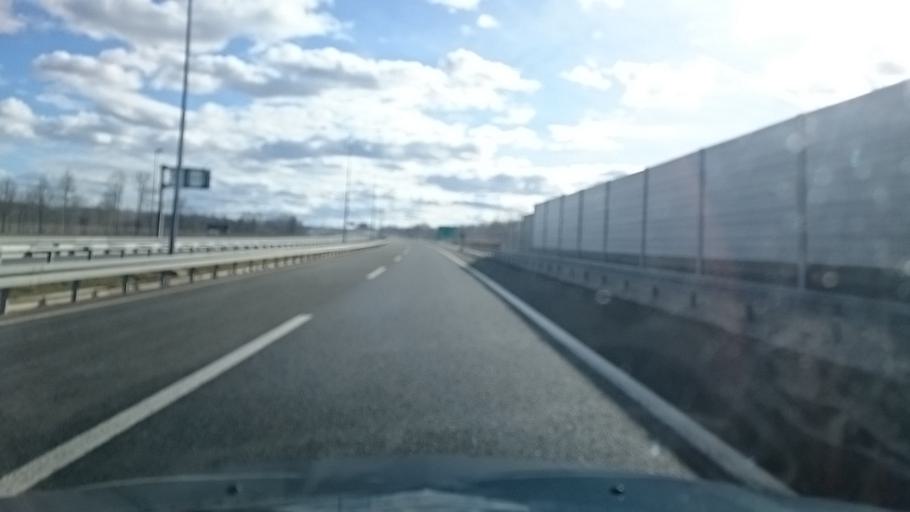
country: BA
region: Republika Srpska
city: Bosanska Gradiska
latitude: 45.0439
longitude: 17.2138
